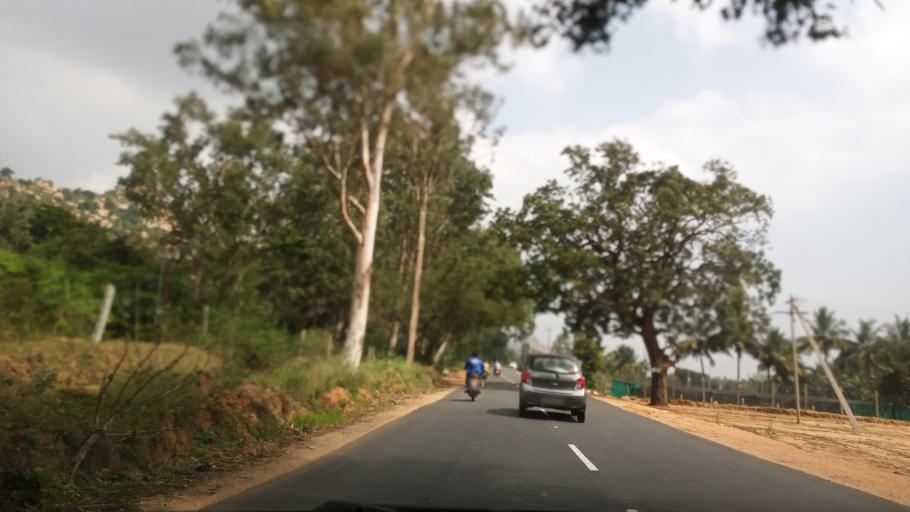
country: IN
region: Andhra Pradesh
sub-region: Chittoor
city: Madanapalle
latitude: 13.6366
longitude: 78.5915
